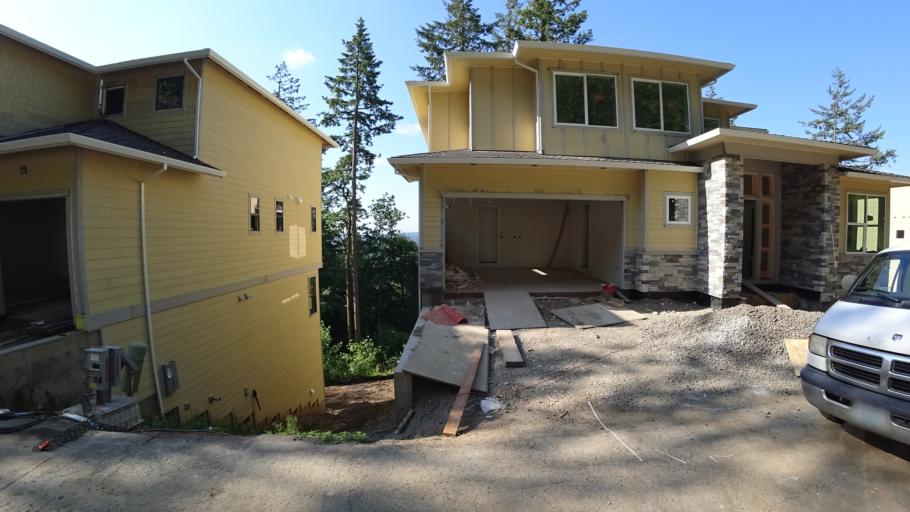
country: US
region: Oregon
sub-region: Washington County
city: West Slope
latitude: 45.5003
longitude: -122.7227
